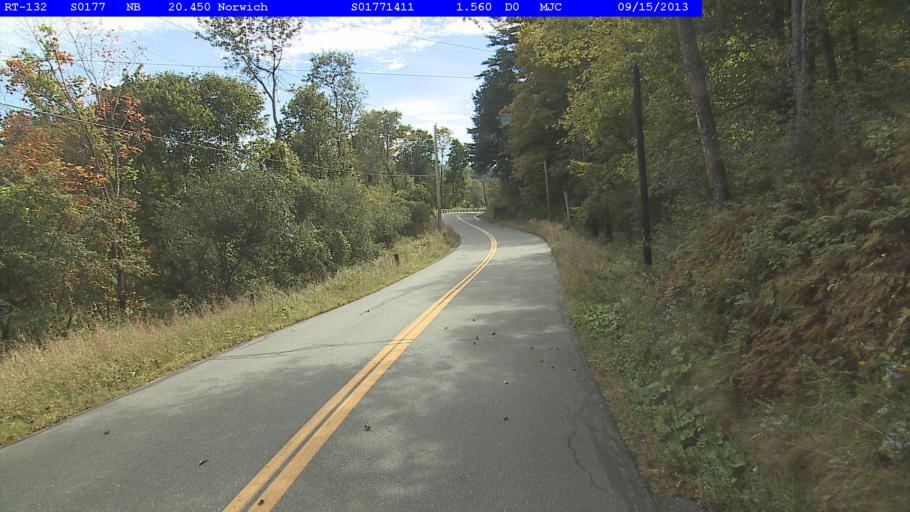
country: US
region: New Hampshire
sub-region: Grafton County
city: Hanover
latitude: 43.7683
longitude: -72.2473
